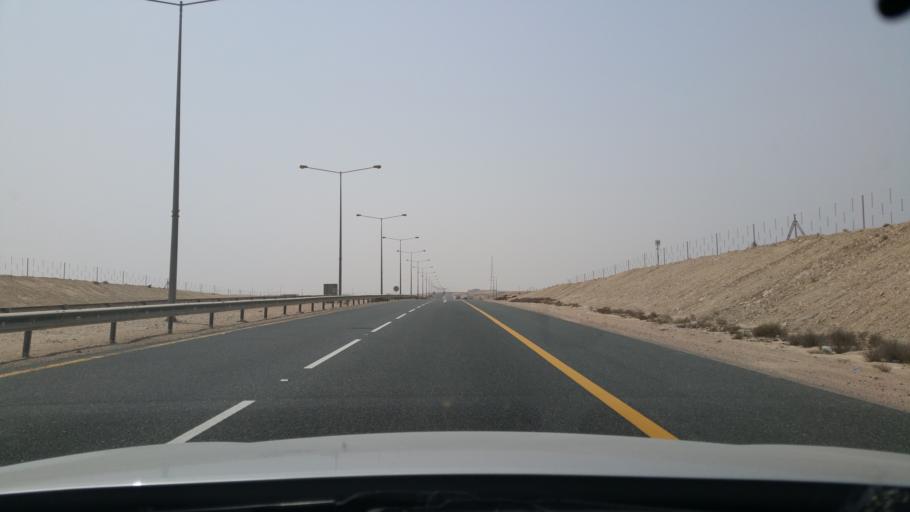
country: QA
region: Baladiyat ar Rayyan
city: Dukhan
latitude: 25.3279
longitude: 50.7861
